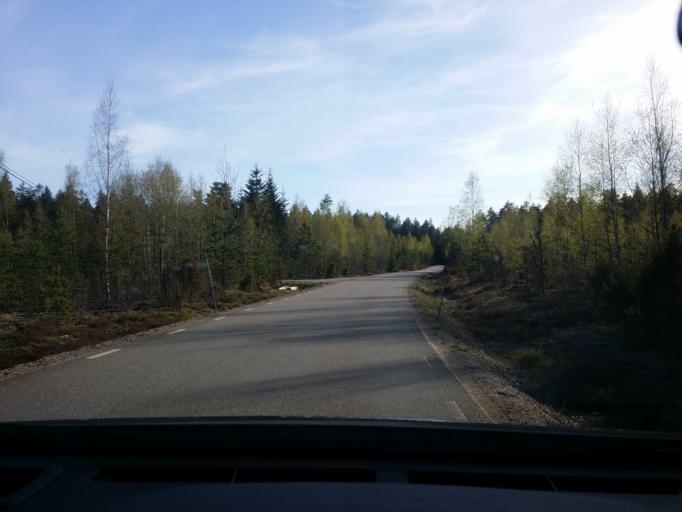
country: SE
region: Dalarna
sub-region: Avesta Kommun
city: Avesta
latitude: 60.0659
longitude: 16.3440
